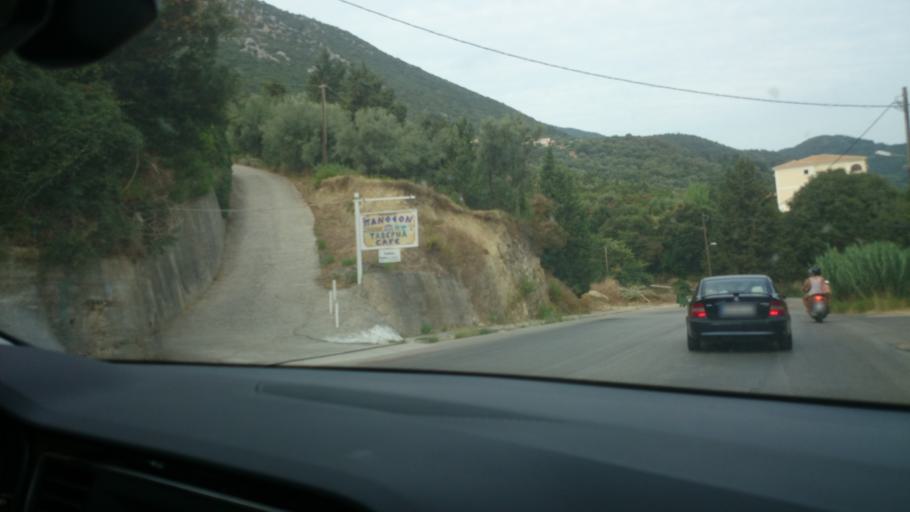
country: GR
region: Ionian Islands
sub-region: Lefkada
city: Nidri
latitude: 38.7488
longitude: 20.7247
